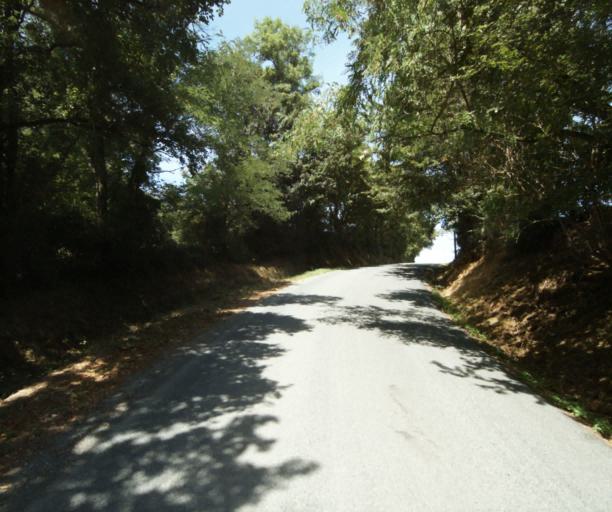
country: FR
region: Midi-Pyrenees
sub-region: Departement de la Haute-Garonne
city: Revel
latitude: 43.4960
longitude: 2.0212
